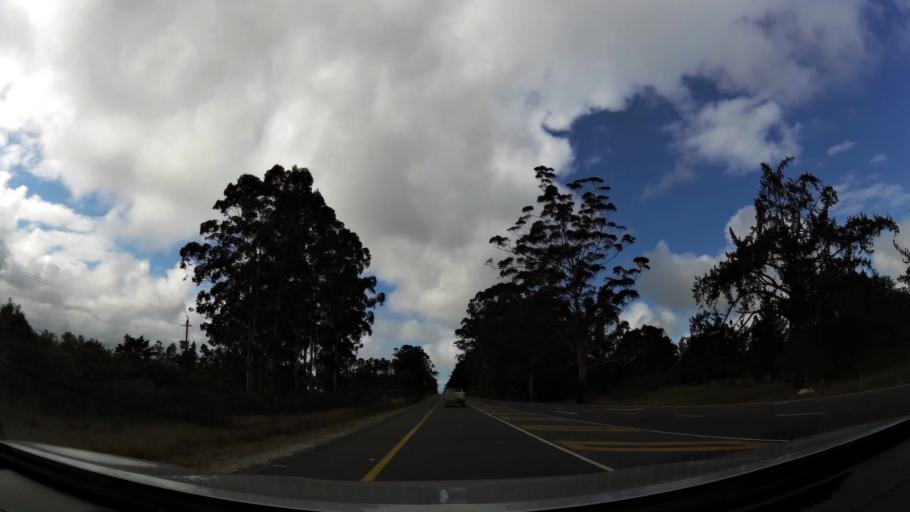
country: ZA
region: Western Cape
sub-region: Eden District Municipality
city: Plettenberg Bay
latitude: -34.0443
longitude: 23.2864
